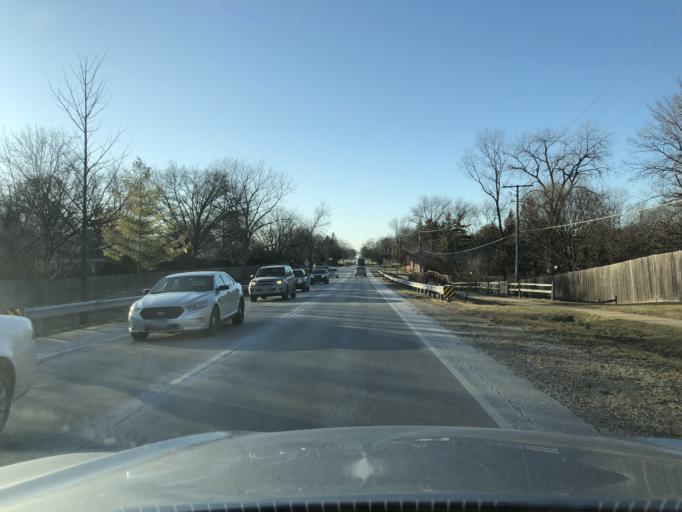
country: US
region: Illinois
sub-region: Cook County
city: Barrington
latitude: 42.1542
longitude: -88.1125
